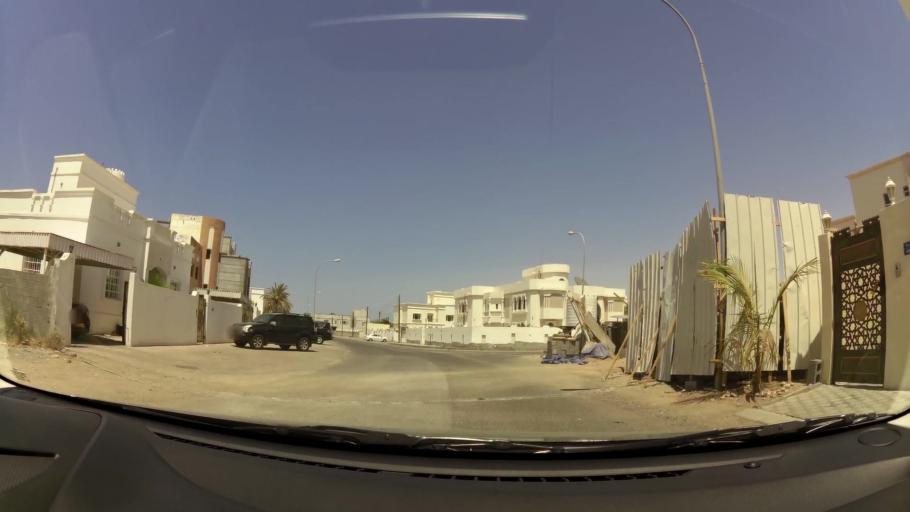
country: OM
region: Muhafazat Masqat
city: As Sib al Jadidah
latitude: 23.6202
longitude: 58.2281
